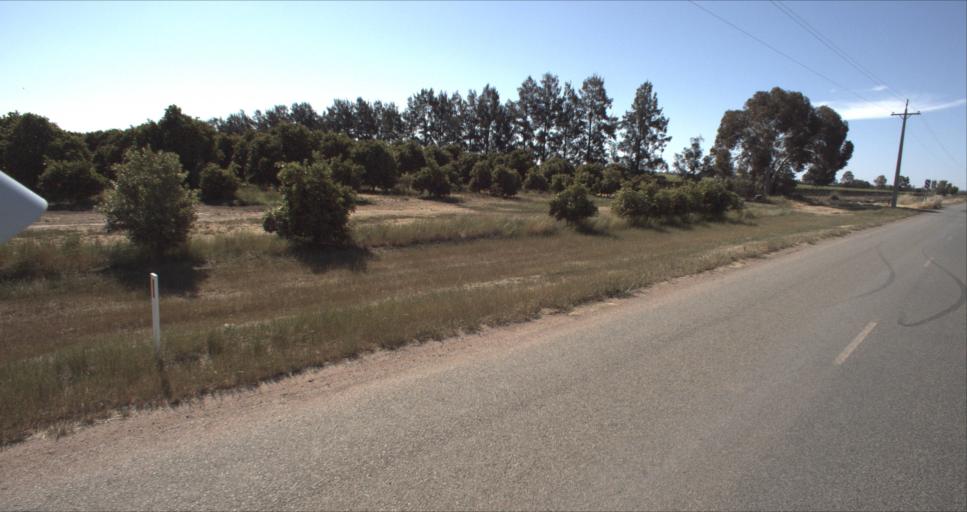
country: AU
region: New South Wales
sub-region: Leeton
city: Leeton
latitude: -34.5852
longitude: 146.3791
